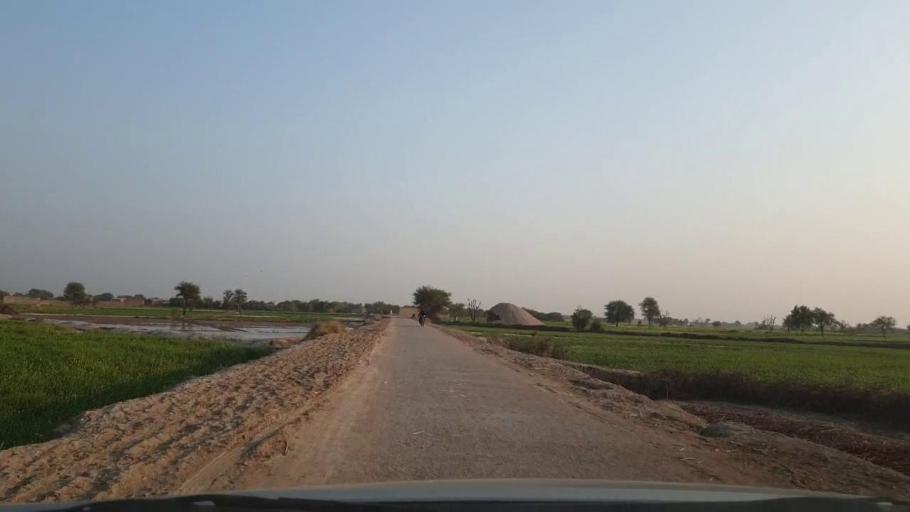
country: PK
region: Sindh
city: Tando Adam
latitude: 25.7084
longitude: 68.6039
